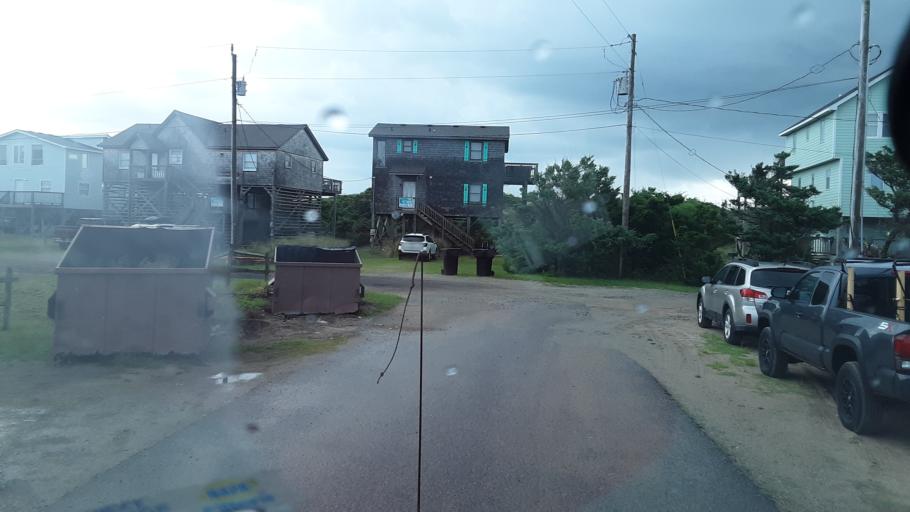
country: US
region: North Carolina
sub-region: Dare County
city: Buxton
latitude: 35.3519
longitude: -75.5016
